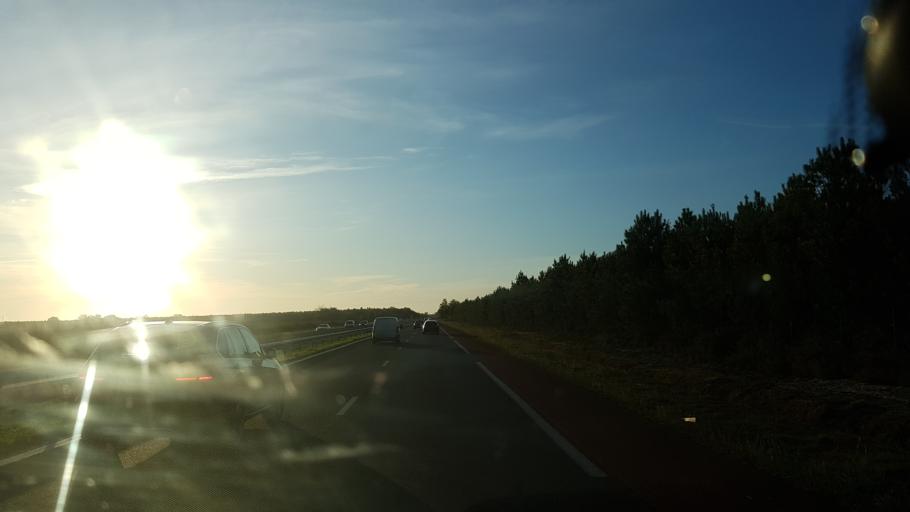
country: FR
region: Aquitaine
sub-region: Departement de la Gironde
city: Lanton
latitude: 44.7786
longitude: -1.0076
